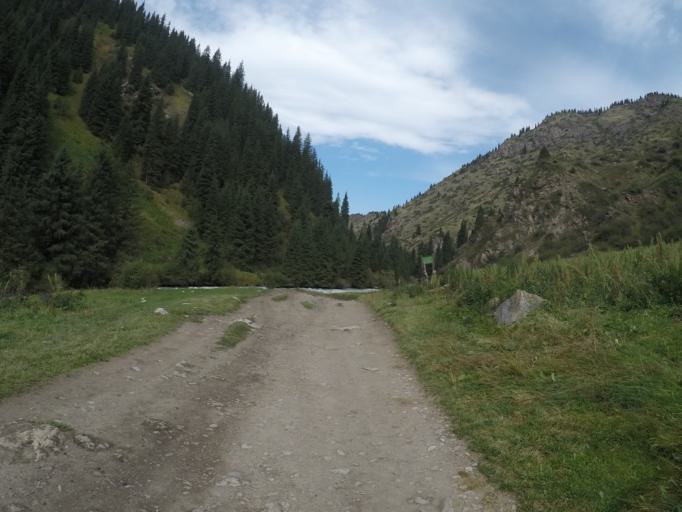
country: KG
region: Ysyk-Koel
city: Teploklyuchenka
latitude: 42.4390
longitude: 78.5585
